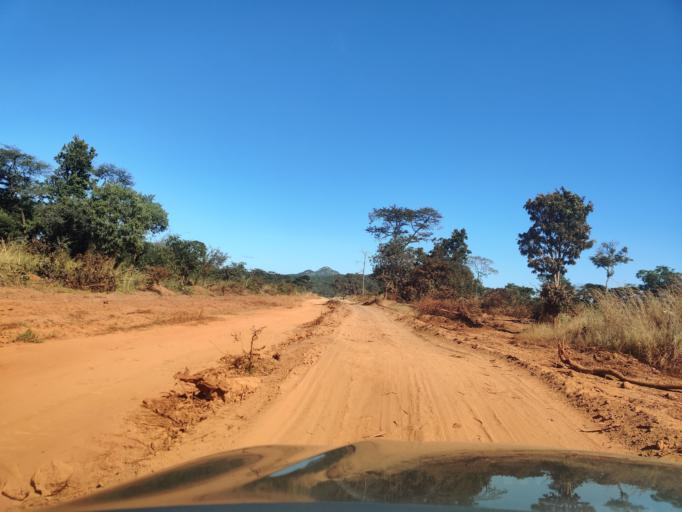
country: ZM
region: Central
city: Kapiri Mposhi
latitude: -13.5264
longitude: 28.8799
